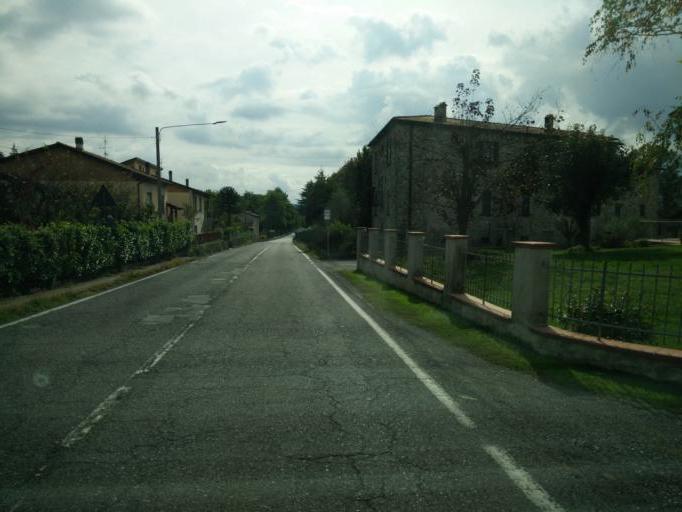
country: IT
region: Tuscany
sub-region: Provincia di Massa-Carrara
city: Filattiera
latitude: 44.3261
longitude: 9.9394
